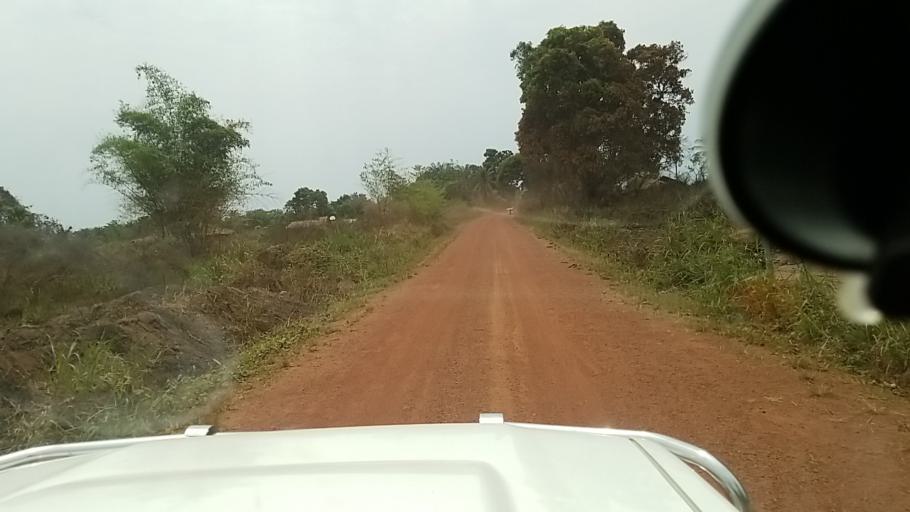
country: CD
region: Equateur
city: Libenge
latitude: 3.7341
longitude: 18.7768
